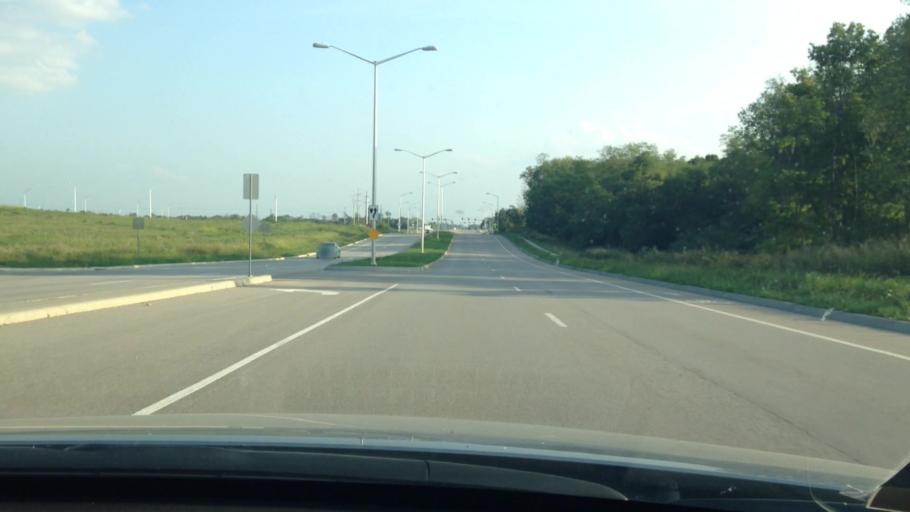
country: US
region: Missouri
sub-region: Platte County
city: Weatherby Lake
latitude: 39.2599
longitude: -94.6310
